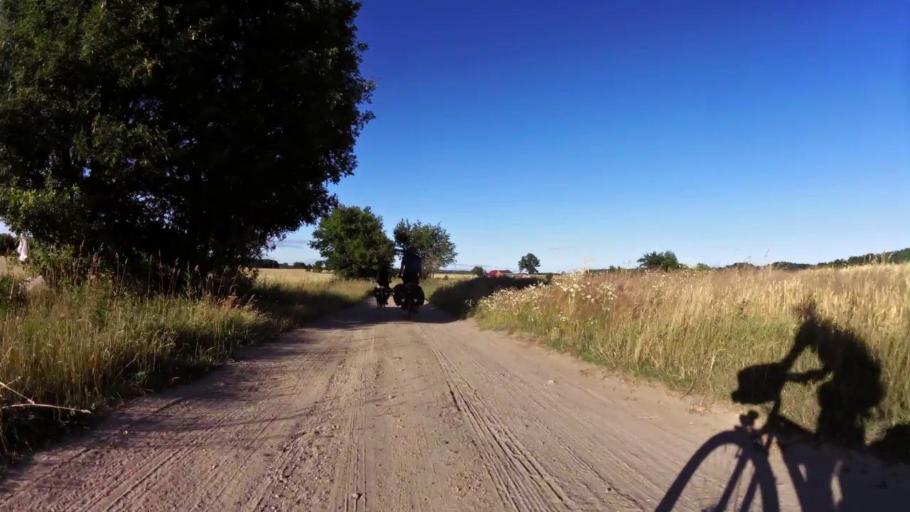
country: PL
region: West Pomeranian Voivodeship
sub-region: Powiat swidwinski
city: Swidwin
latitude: 53.7308
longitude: 15.8451
